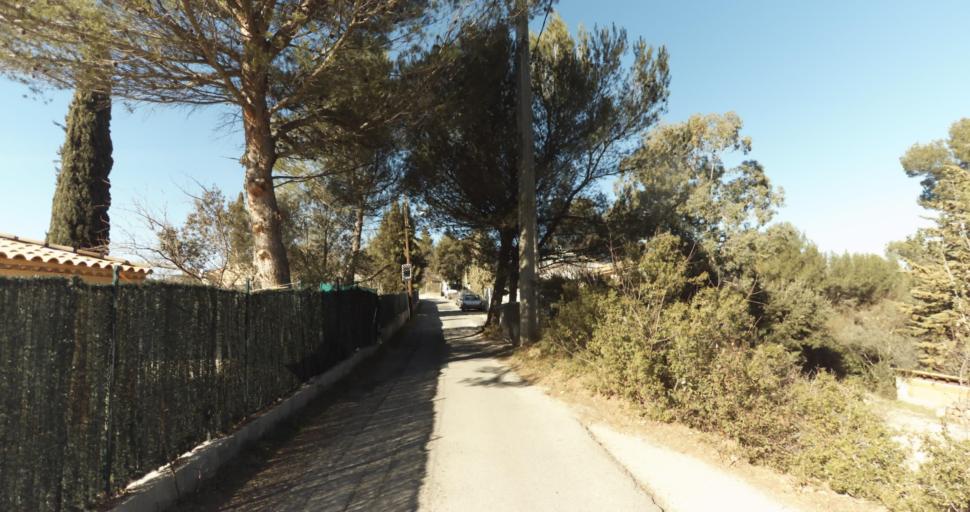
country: FR
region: Provence-Alpes-Cote d'Azur
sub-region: Departement des Bouches-du-Rhone
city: La Bouilladisse
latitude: 43.3882
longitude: 5.5890
